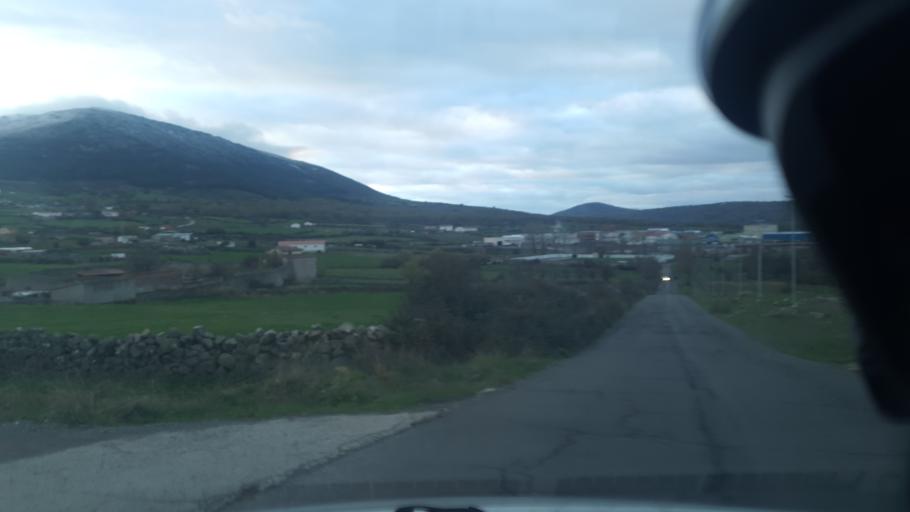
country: ES
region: Castille and Leon
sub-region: Provincia de Segovia
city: Vegas de Matute
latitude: 40.7227
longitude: -4.2508
